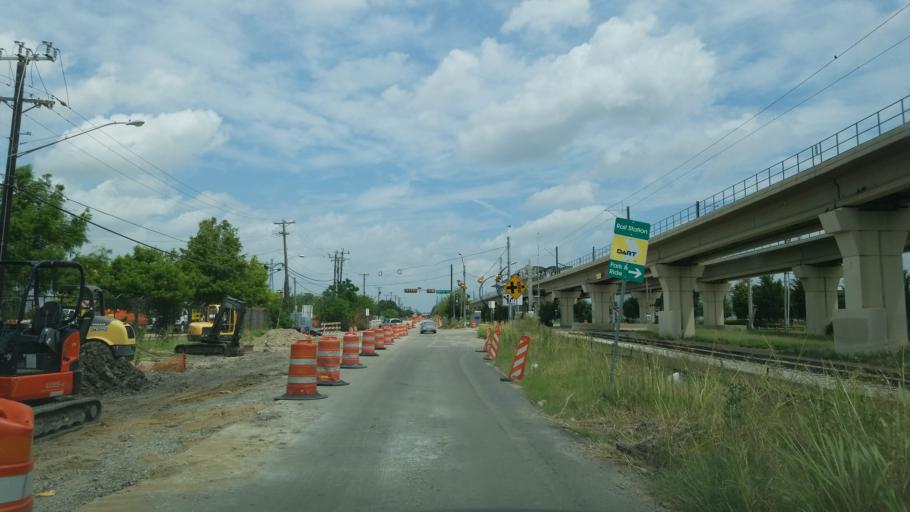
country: US
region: Texas
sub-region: Dallas County
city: Farmers Branch
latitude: 32.8803
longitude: -96.8836
